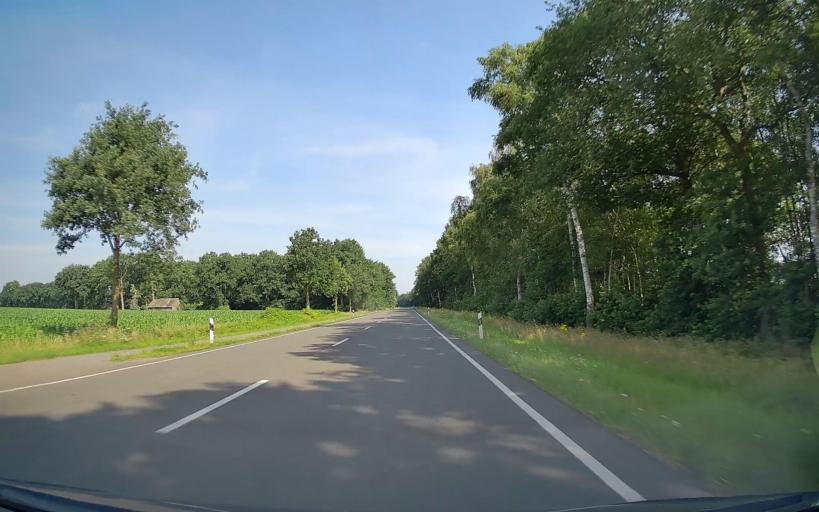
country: DE
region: Lower Saxony
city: Bosel
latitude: 52.9503
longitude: 7.9350
